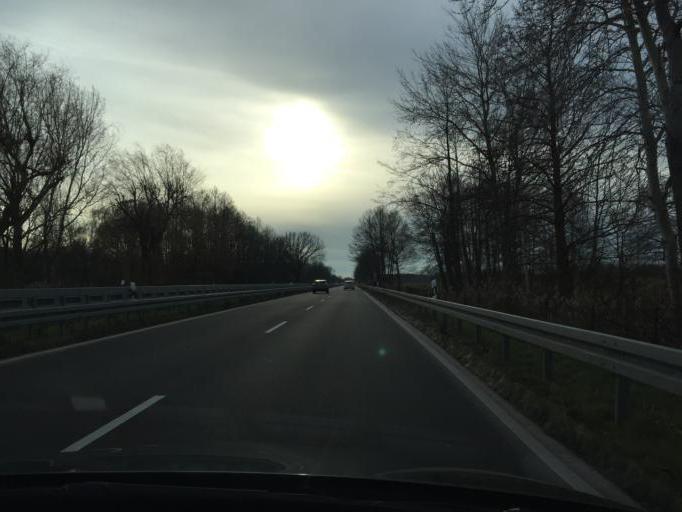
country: DE
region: Brandenburg
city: Peitz
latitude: 51.8331
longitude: 14.3872
